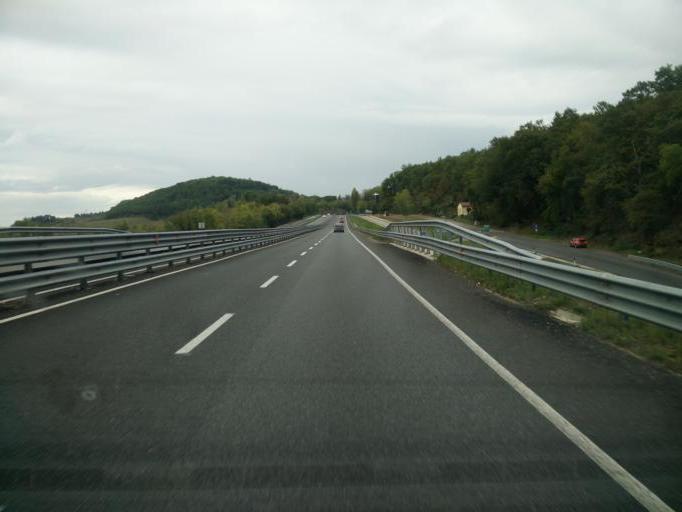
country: IT
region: Tuscany
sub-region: Provincia di Siena
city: Bellavista
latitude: 43.4323
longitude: 11.1447
